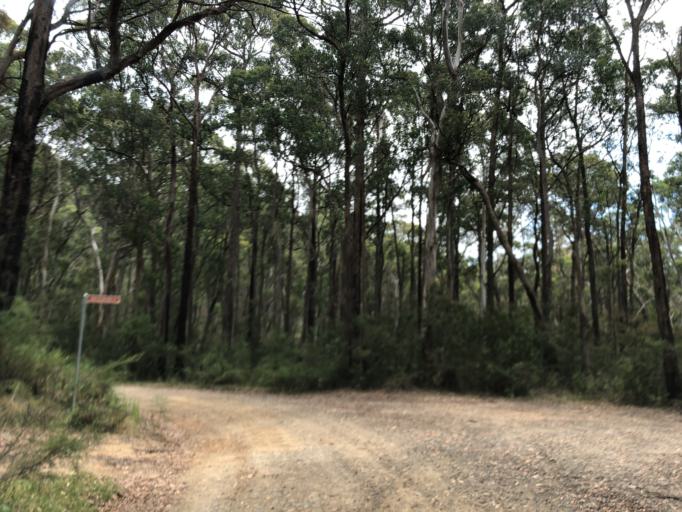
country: AU
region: Victoria
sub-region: Moorabool
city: Bacchus Marsh
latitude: -37.4691
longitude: 144.2818
